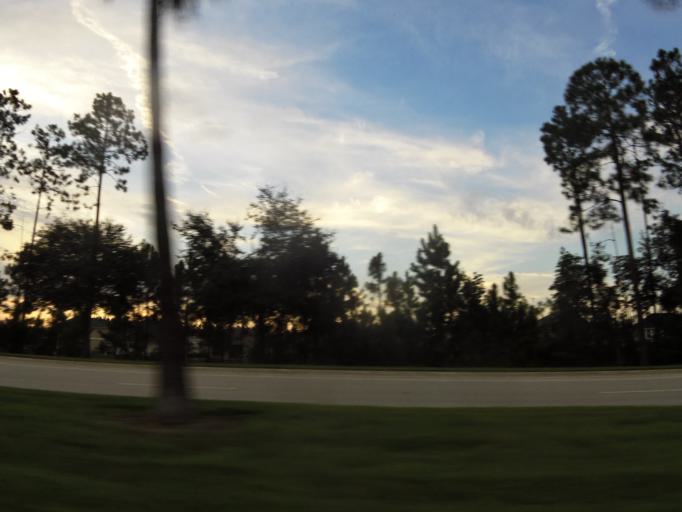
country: US
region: Florida
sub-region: Saint Johns County
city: Fruit Cove
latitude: 30.0819
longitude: -81.5487
